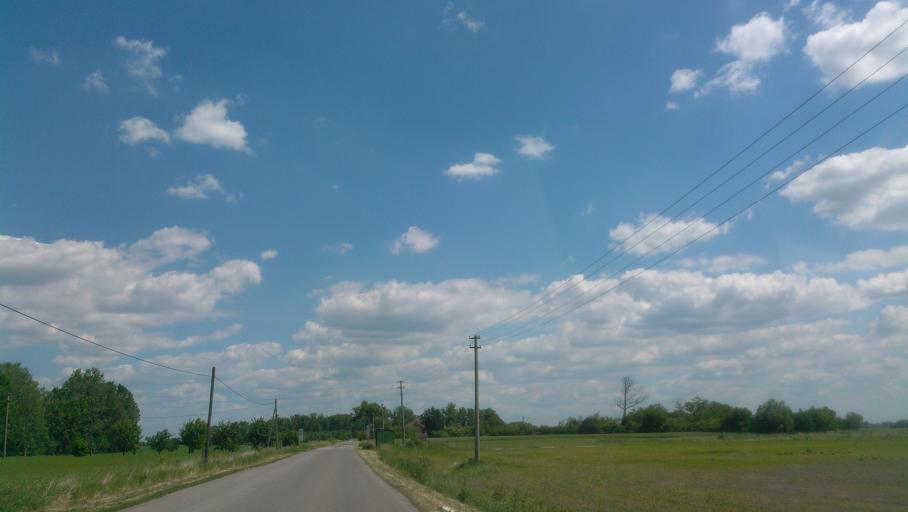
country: SK
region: Nitriansky
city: Kolarovo
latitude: 47.8857
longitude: 17.9010
